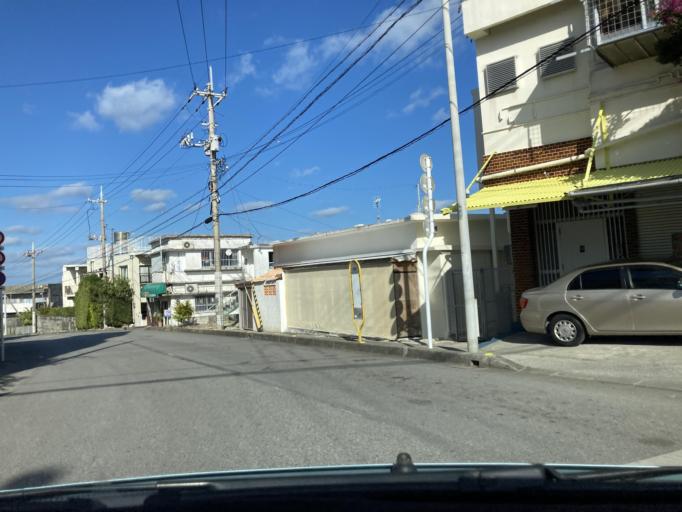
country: JP
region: Okinawa
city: Katsuren-haebaru
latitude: 26.3090
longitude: 127.9119
